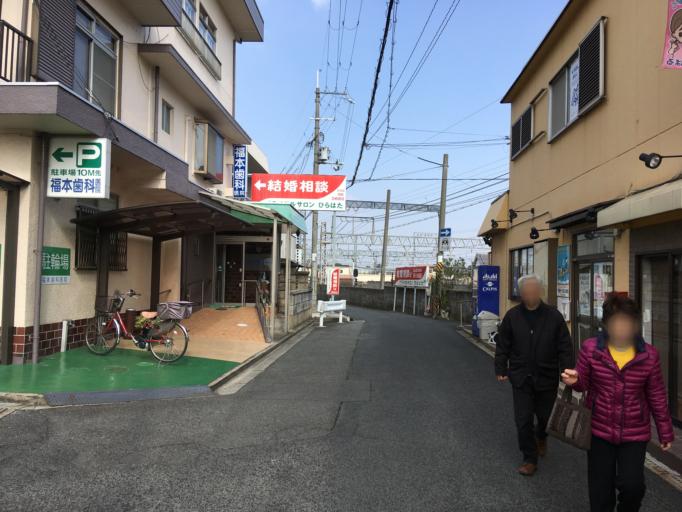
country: JP
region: Nara
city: Tawaramoto
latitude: 34.6068
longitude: 135.7824
